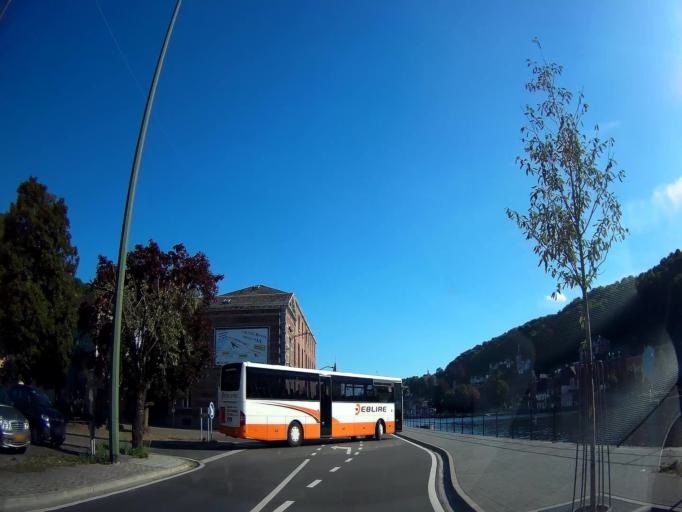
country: BE
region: Wallonia
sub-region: Province de Namur
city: Dinant
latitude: 50.2669
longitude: 4.9066
